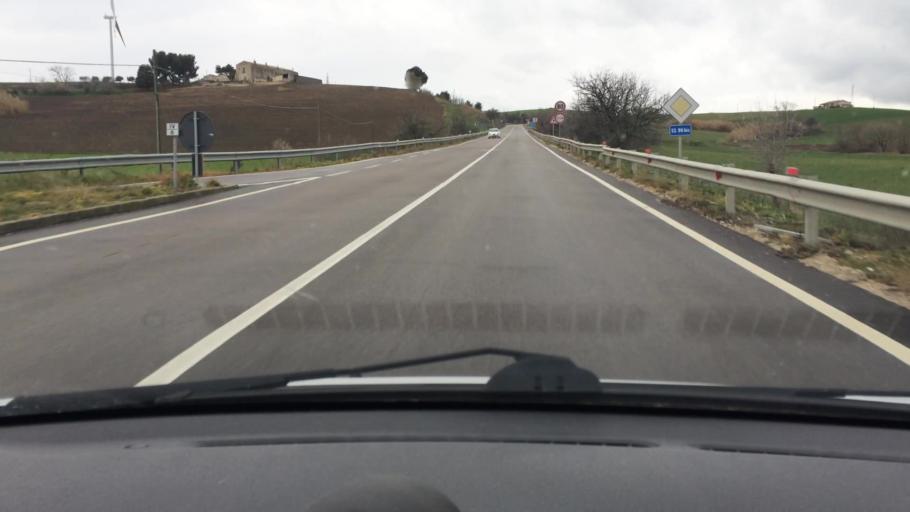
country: IT
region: Basilicate
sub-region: Provincia di Potenza
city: San Chirico Nuovo
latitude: 40.7663
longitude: 16.1027
